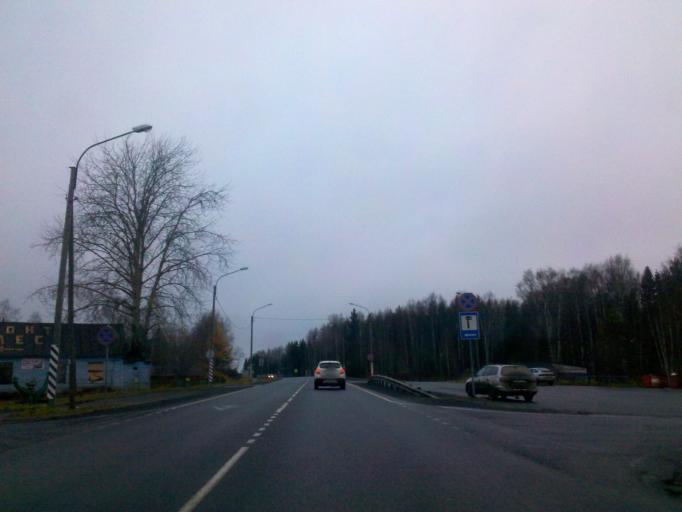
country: RU
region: Republic of Karelia
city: Shuya
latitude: 61.8199
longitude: 34.0824
